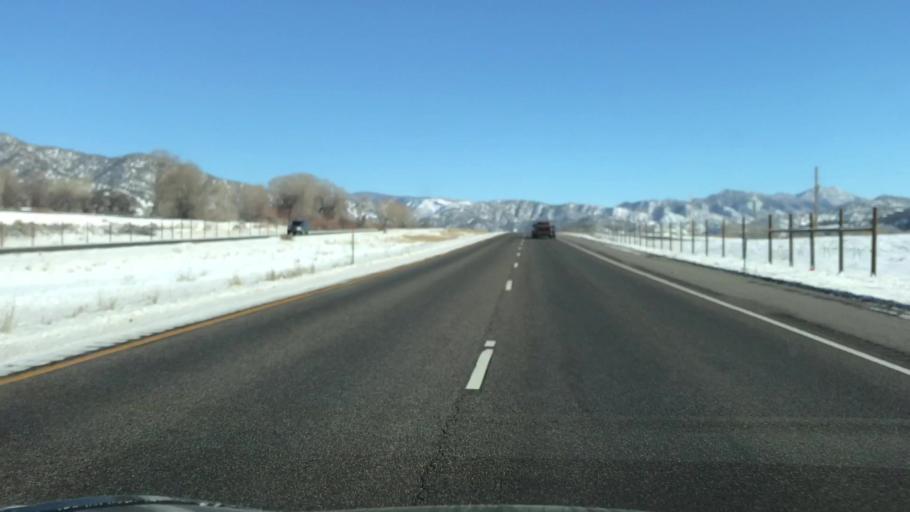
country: US
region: Colorado
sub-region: Garfield County
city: New Castle
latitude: 39.5514
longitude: -107.5923
